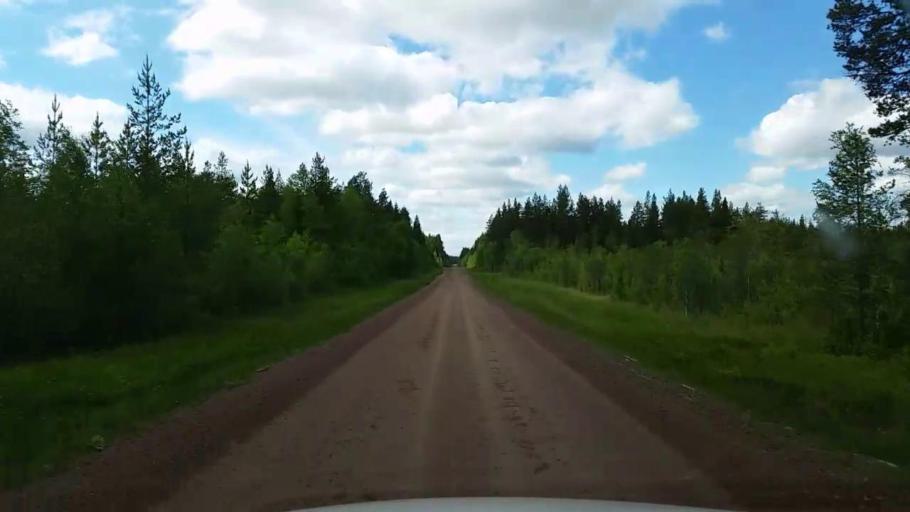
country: SE
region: Gaevleborg
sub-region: Ovanakers Kommun
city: Alfta
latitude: 61.4698
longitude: 16.0232
